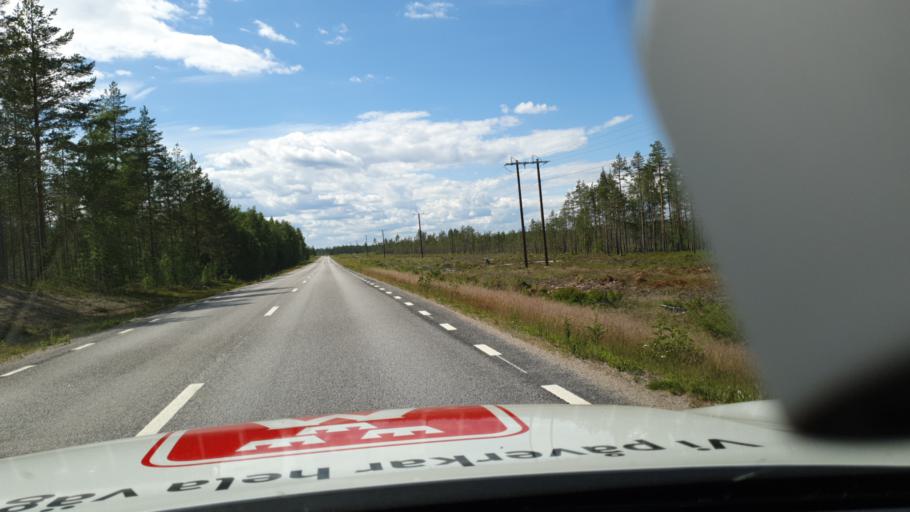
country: SE
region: Jaemtland
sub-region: Harjedalens Kommun
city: Sveg
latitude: 62.0307
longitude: 14.7080
